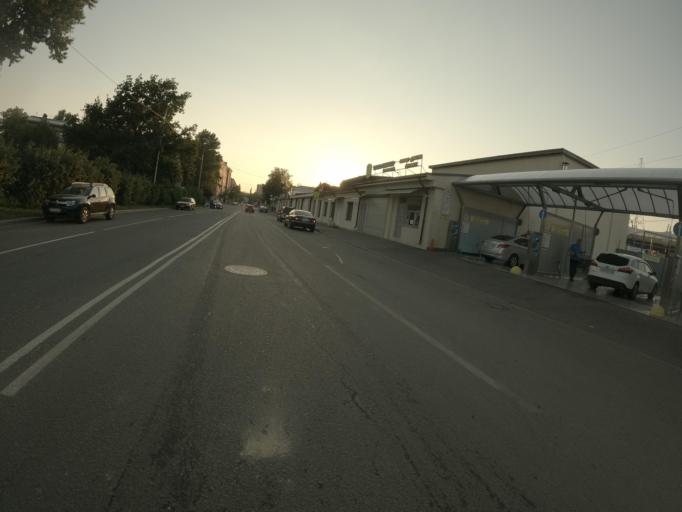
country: RU
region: St.-Petersburg
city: Avtovo
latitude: 59.8802
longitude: 30.2789
